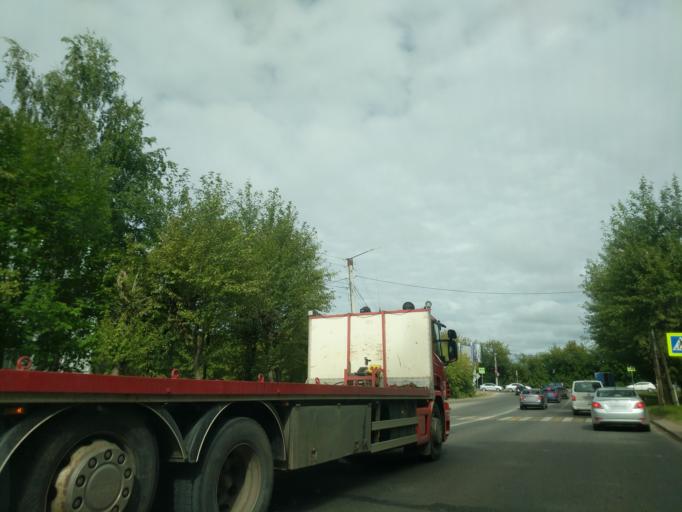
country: RU
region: Kirov
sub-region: Kirovo-Chepetskiy Rayon
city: Kirov
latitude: 58.6023
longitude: 49.6445
